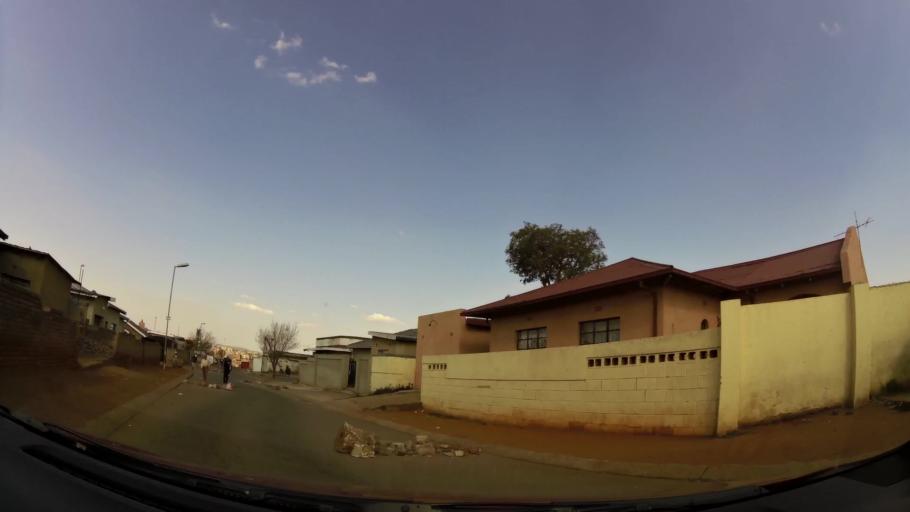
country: ZA
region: Gauteng
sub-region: City of Johannesburg Metropolitan Municipality
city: Soweto
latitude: -26.2303
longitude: 27.8813
